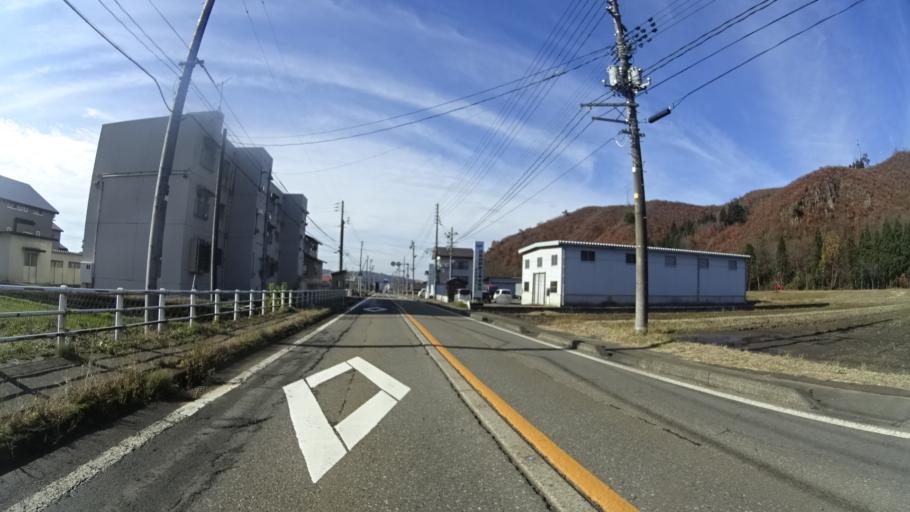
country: JP
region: Niigata
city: Muikamachi
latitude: 37.2273
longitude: 138.9979
